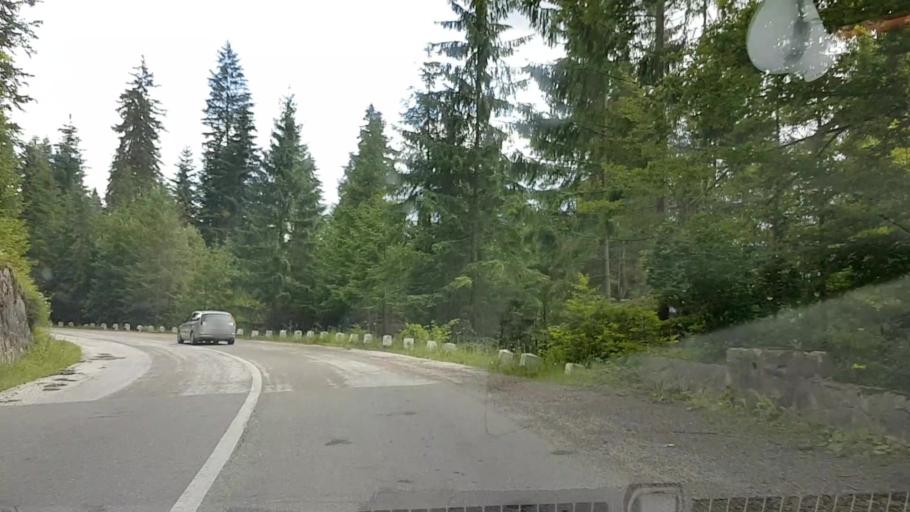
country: RO
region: Neamt
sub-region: Comuna Pangarati
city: Pangarati
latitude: 46.9738
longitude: 26.1164
